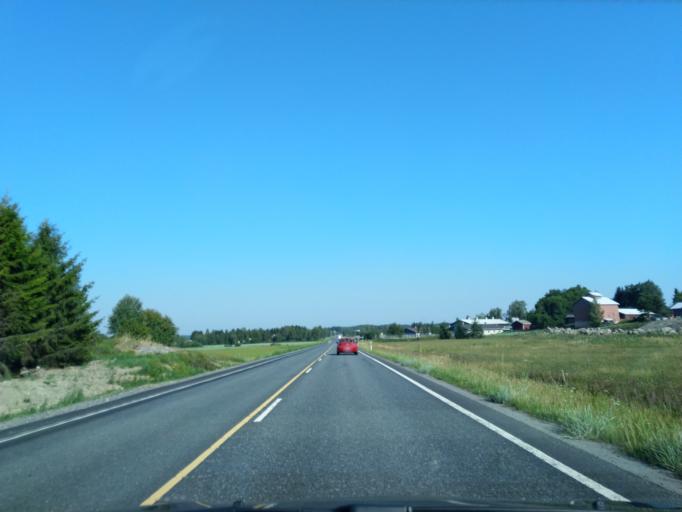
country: FI
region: Haeme
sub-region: Forssa
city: Tammela
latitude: 60.7591
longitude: 23.6987
